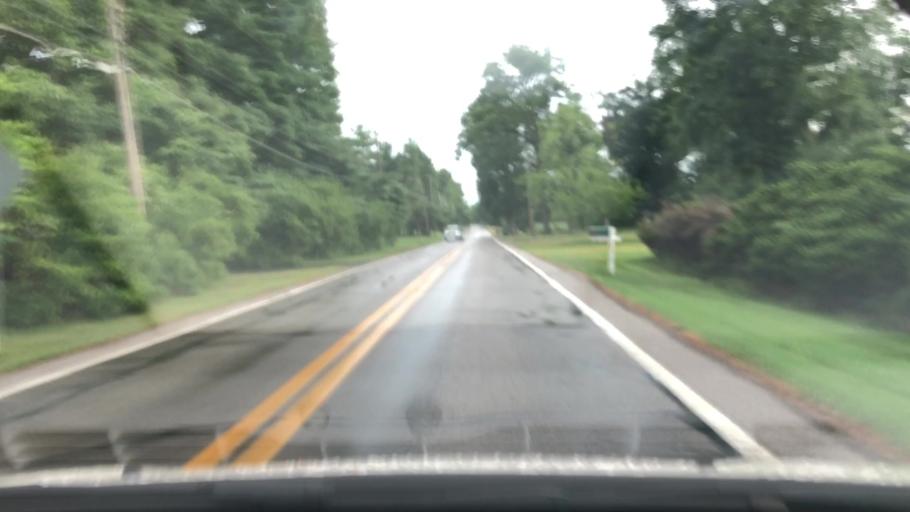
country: US
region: Ohio
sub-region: Franklin County
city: New Albany
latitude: 40.1133
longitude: -82.8564
